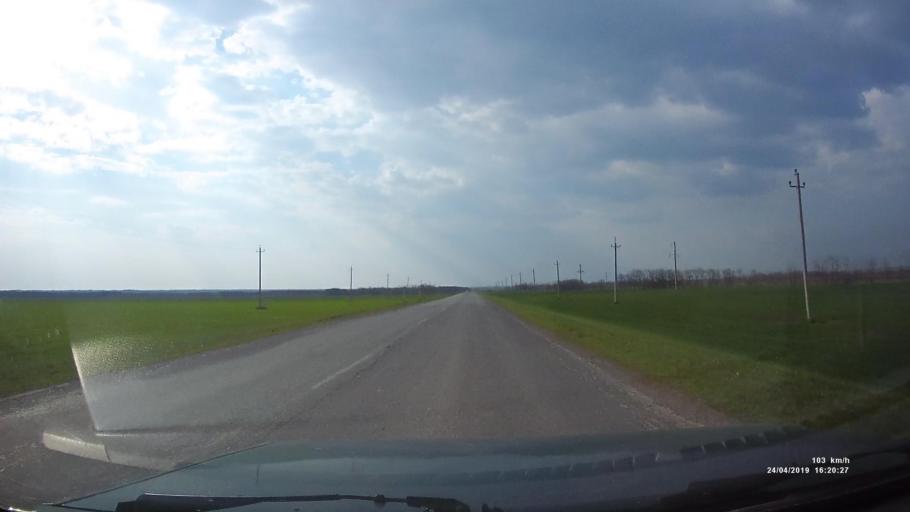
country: RU
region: Rostov
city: Orlovskiy
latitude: 46.7931
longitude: 42.0794
